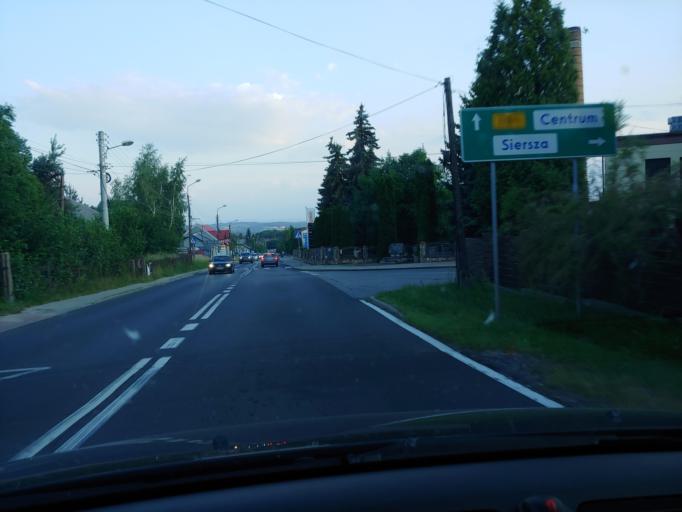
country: PL
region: Lesser Poland Voivodeship
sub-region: Powiat chrzanowski
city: Myslachowice
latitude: 50.1741
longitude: 19.4733
